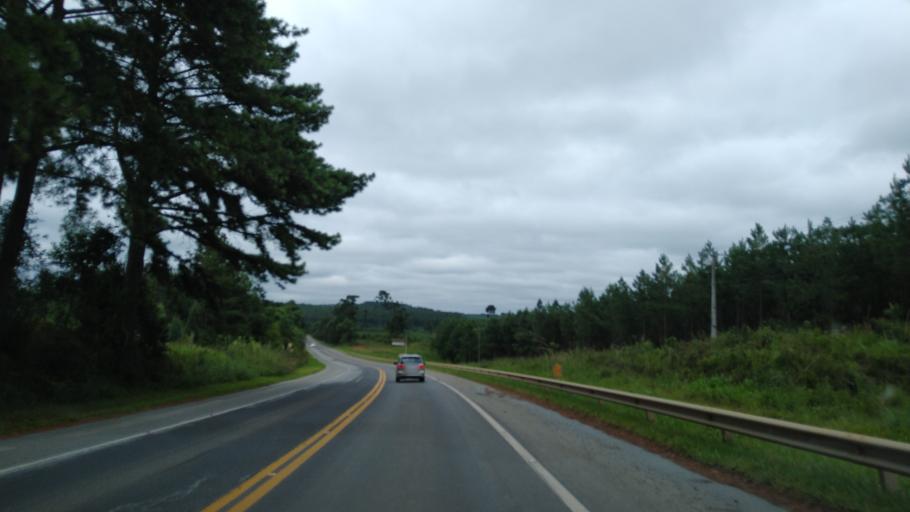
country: BR
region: Santa Catarina
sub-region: Tres Barras
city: Tres Barras
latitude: -26.1613
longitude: -50.1334
